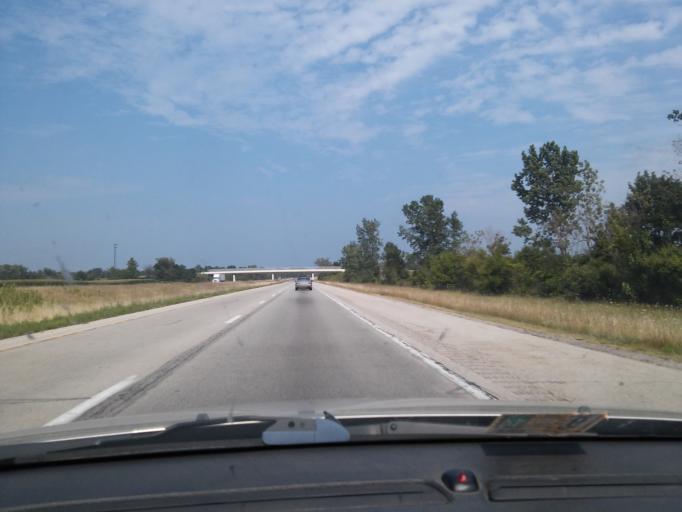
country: US
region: Ohio
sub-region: Preble County
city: New Paris
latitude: 39.8314
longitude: -84.7276
